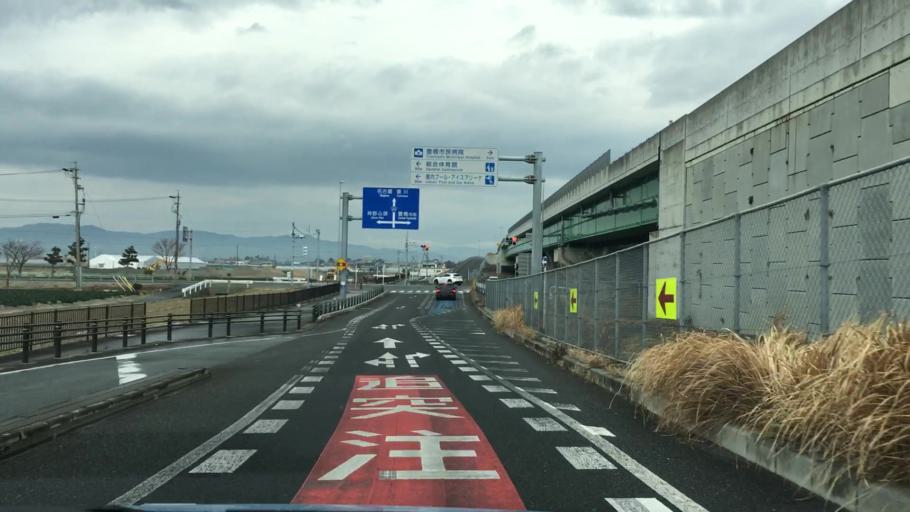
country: JP
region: Aichi
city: Kozakai-cho
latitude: 34.7603
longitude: 137.3328
